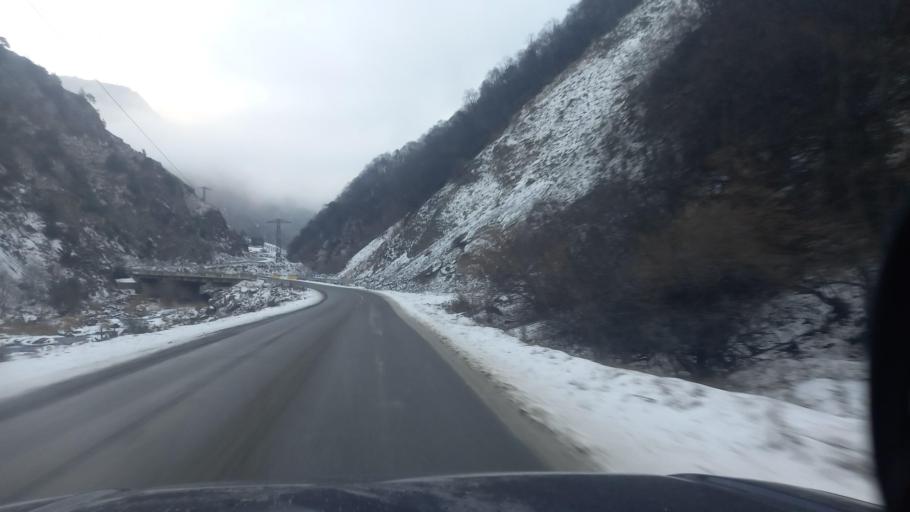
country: RU
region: Ingushetiya
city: Dzhayrakh
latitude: 42.7906
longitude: 44.7707
